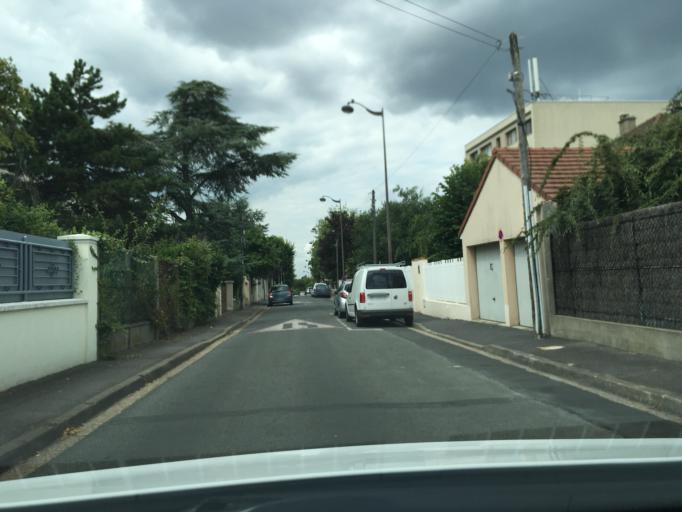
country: FR
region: Ile-de-France
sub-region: Departement des Hauts-de-Seine
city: Rueil-Malmaison
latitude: 48.8690
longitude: 2.1791
